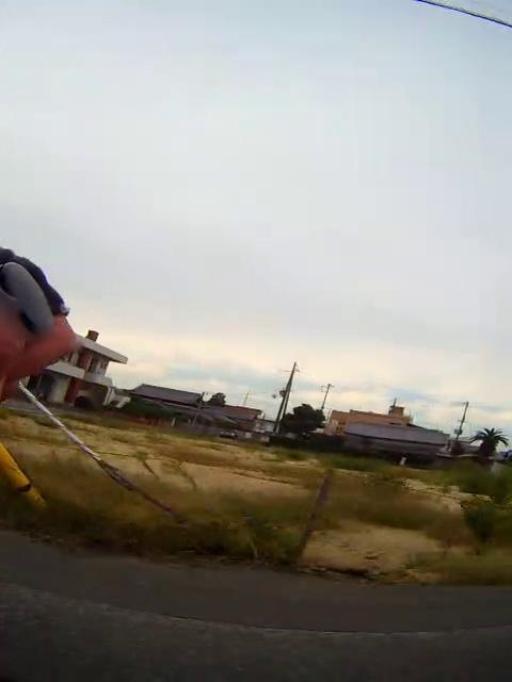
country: JP
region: Hyogo
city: Fukura
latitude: 34.2850
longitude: 134.7751
